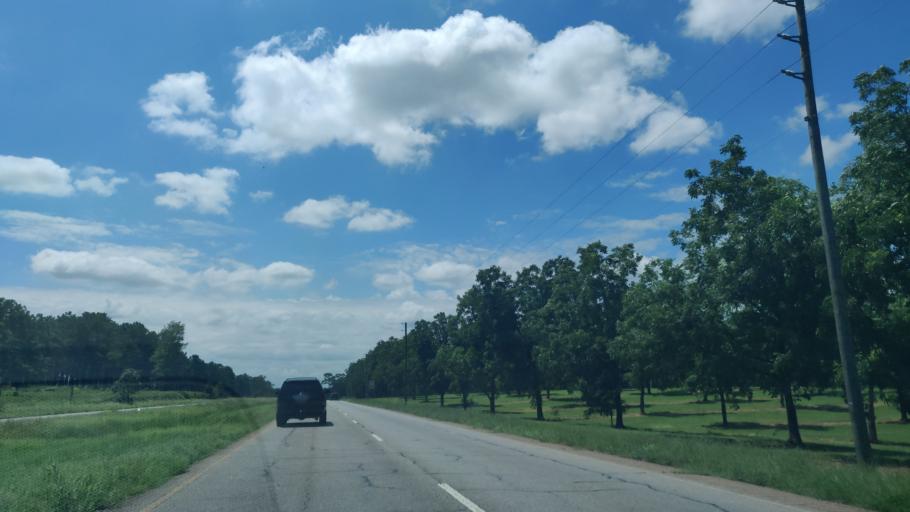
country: US
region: Georgia
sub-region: Stewart County
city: Richland
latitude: 32.0343
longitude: -84.6766
